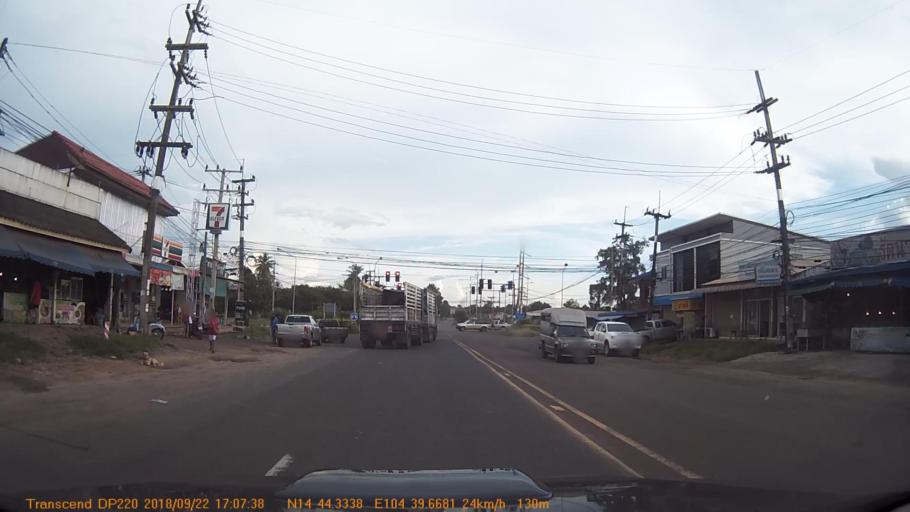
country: TH
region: Sisaket
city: Benchalak
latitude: 14.7390
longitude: 104.6611
